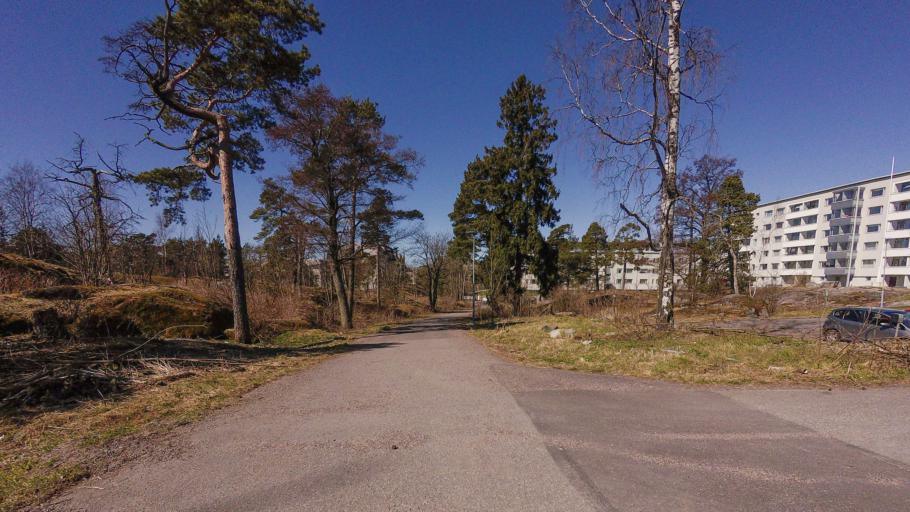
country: FI
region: Uusimaa
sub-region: Helsinki
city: Helsinki
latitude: 60.1690
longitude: 25.0401
